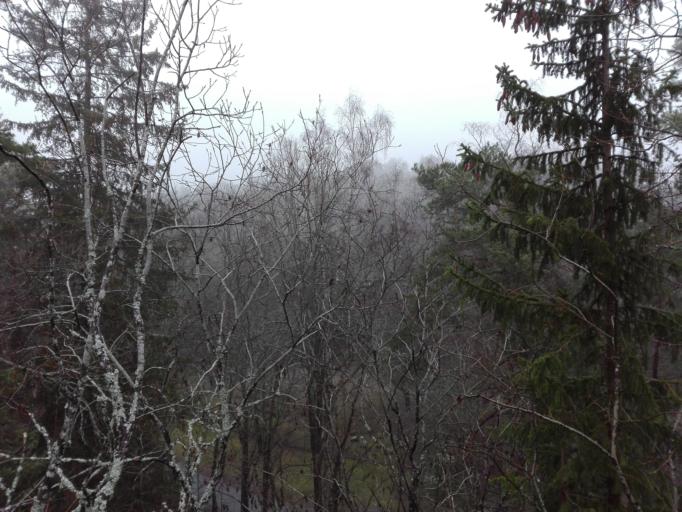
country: SE
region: Stockholm
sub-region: Nacka Kommun
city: Fisksatra
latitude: 59.2904
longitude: 18.2607
